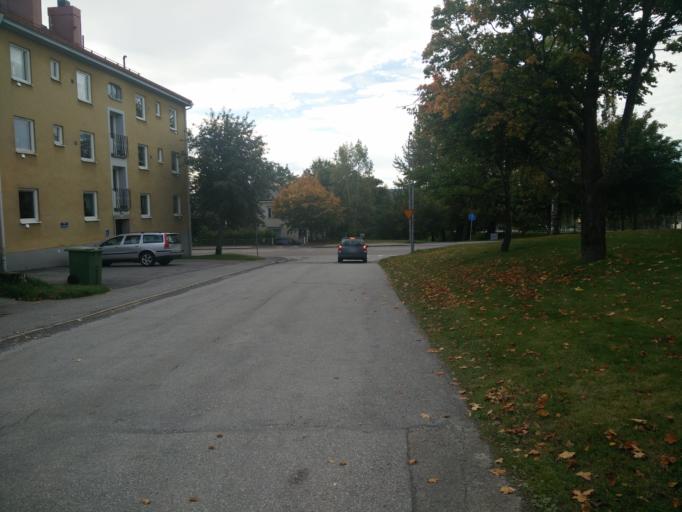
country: SE
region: Vaesternorrland
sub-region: Haernoesands Kommun
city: Haernoesand
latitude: 62.6296
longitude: 17.9443
